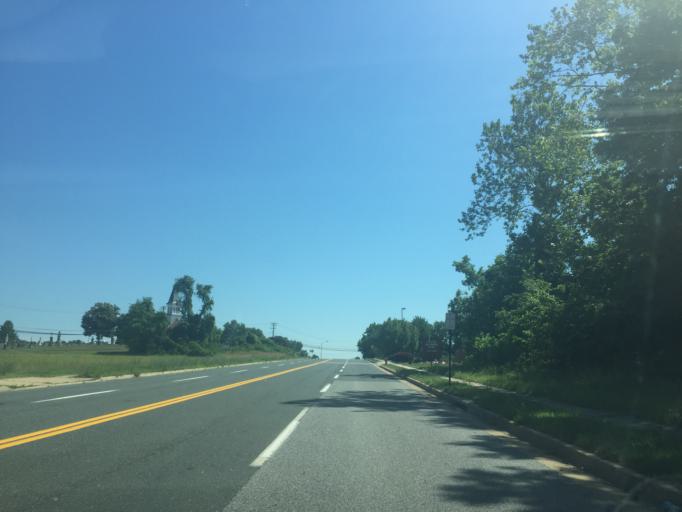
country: US
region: Maryland
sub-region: Baltimore County
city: Rossville
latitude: 39.3292
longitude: -76.4830
